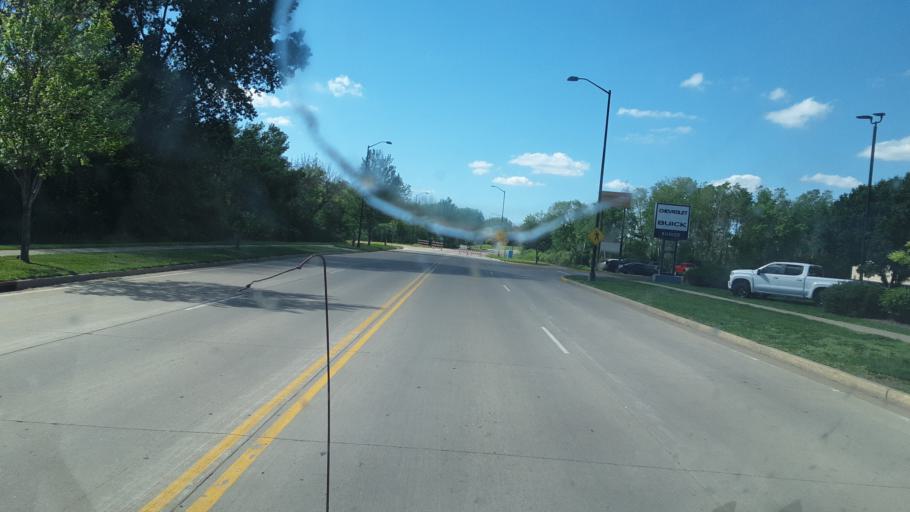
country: US
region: Wisconsin
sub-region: Juneau County
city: Mauston
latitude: 43.8069
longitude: -90.0707
